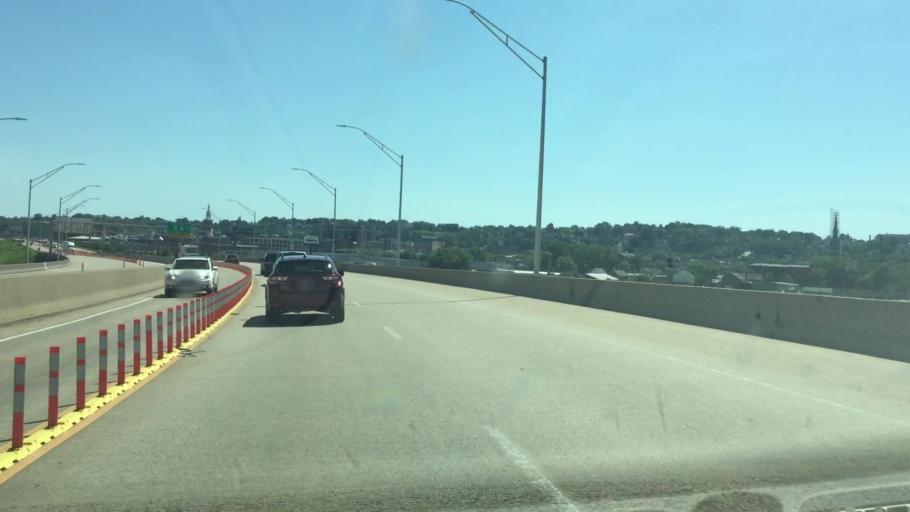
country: US
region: Iowa
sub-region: Dubuque County
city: Dubuque
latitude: 42.5112
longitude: -90.6581
